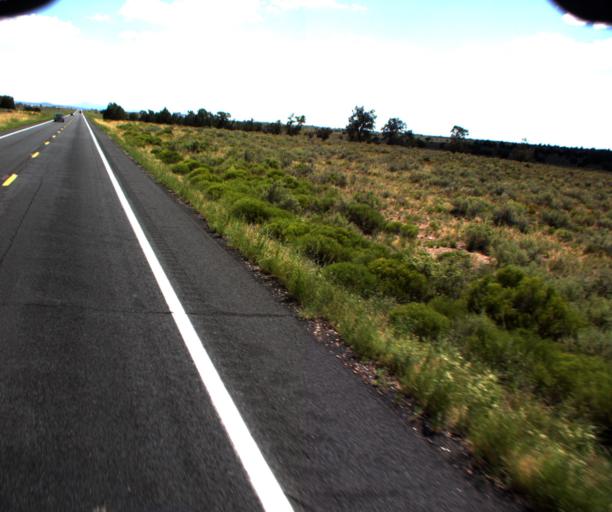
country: US
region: Arizona
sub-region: Coconino County
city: Grand Canyon Village
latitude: 35.6773
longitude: -112.1361
